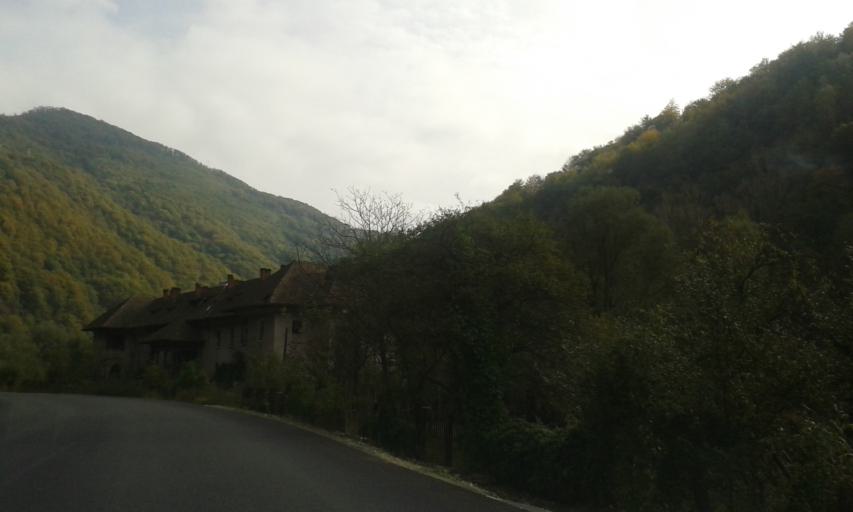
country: RO
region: Gorj
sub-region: Comuna Bumbesti-Jiu
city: Bumbesti-Jiu
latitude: 45.2705
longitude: 23.3781
